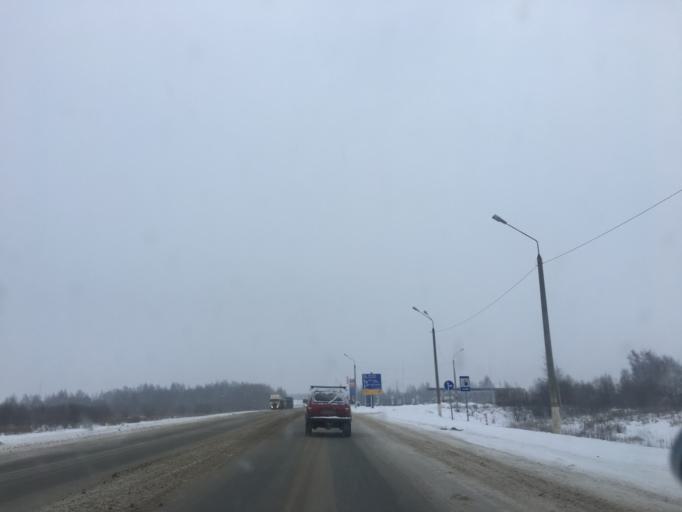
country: RU
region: Tula
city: Kosaya Gora
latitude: 54.1640
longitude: 37.4957
